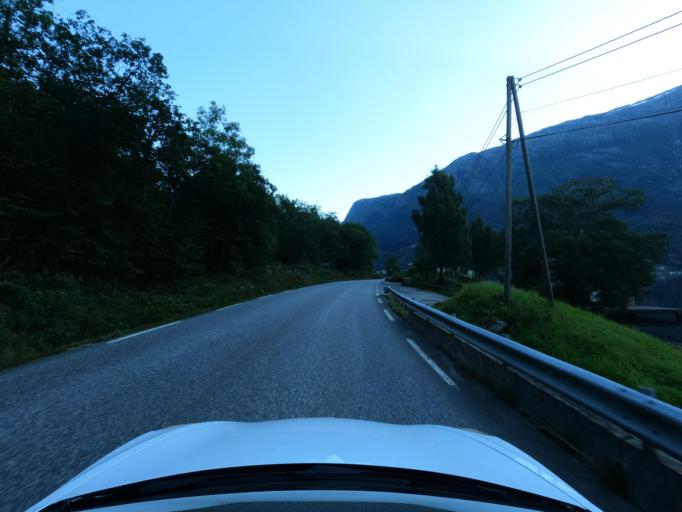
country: NO
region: Hordaland
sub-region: Odda
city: Odda
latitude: 60.0838
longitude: 6.5511
